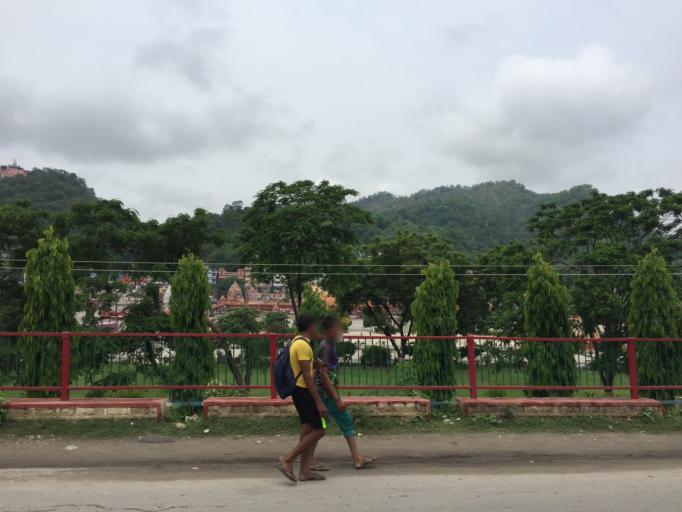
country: IN
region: Uttarakhand
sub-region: Haridwar
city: Haridwar
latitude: 29.9564
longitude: 78.1745
